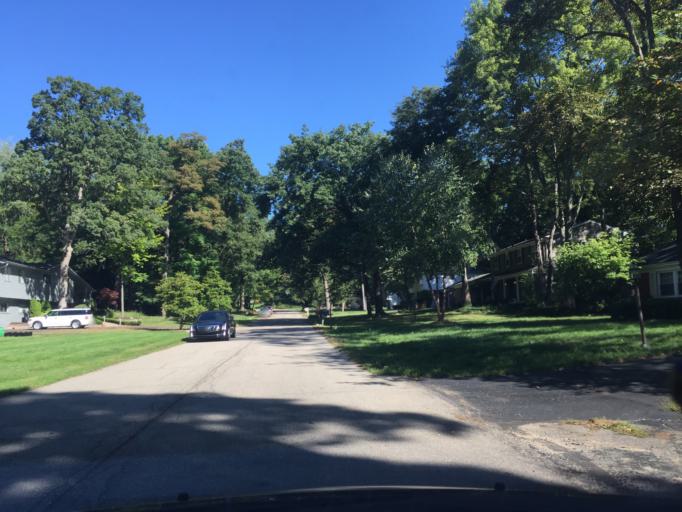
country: US
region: Michigan
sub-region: Oakland County
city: Franklin
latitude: 42.5641
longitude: -83.2911
